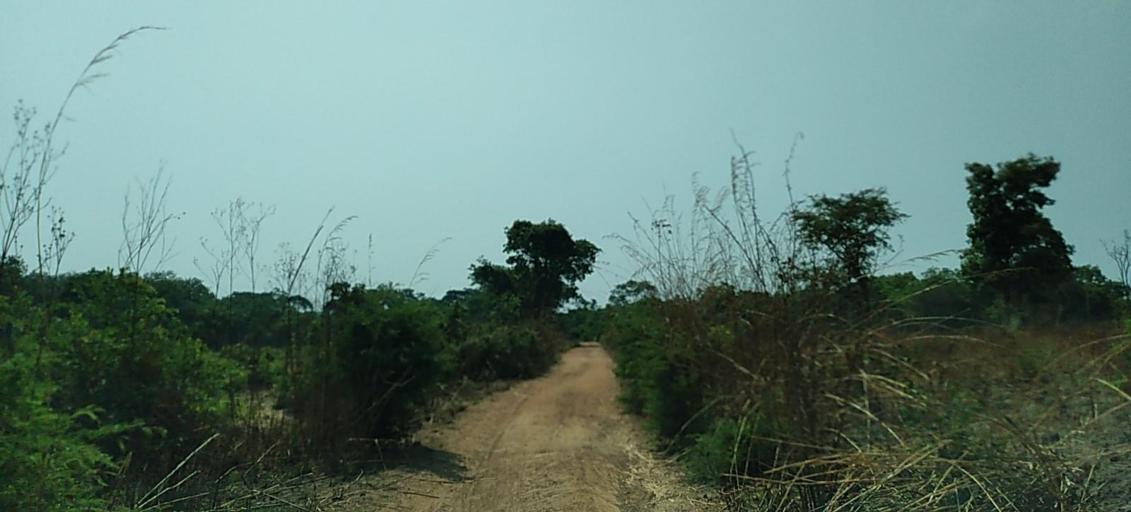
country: ZM
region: Copperbelt
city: Luanshya
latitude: -13.2772
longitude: 28.3061
